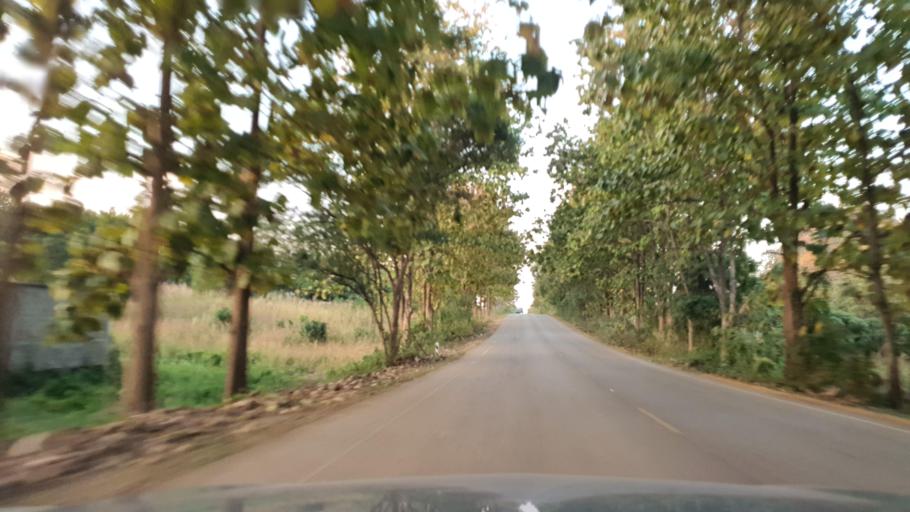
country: TH
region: Phayao
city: Dok Kham Tai
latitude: 19.0075
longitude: 100.0621
